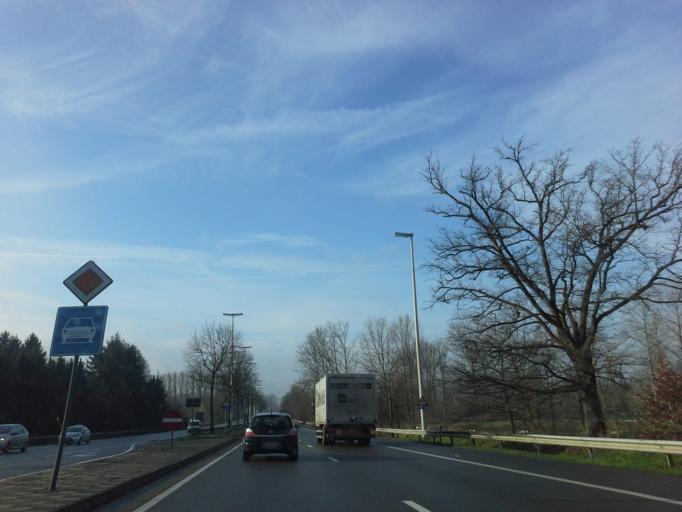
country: BE
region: Flanders
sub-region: Provincie Limburg
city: Alken
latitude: 50.8942
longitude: 5.3152
